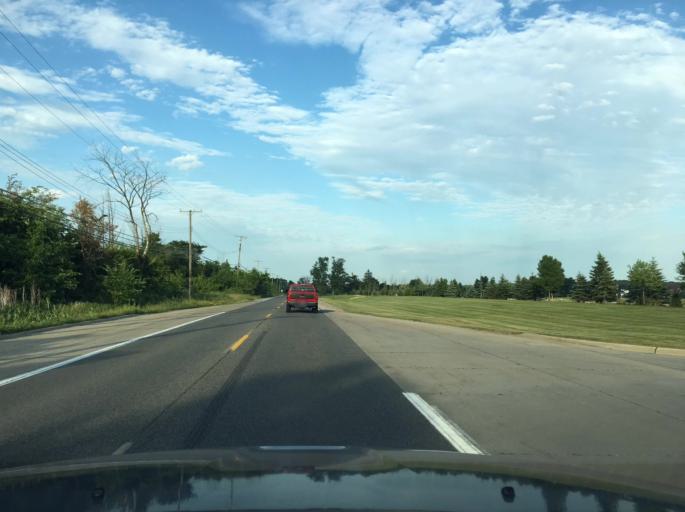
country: US
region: Michigan
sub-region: Macomb County
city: Shelby
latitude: 42.7164
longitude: -82.9444
